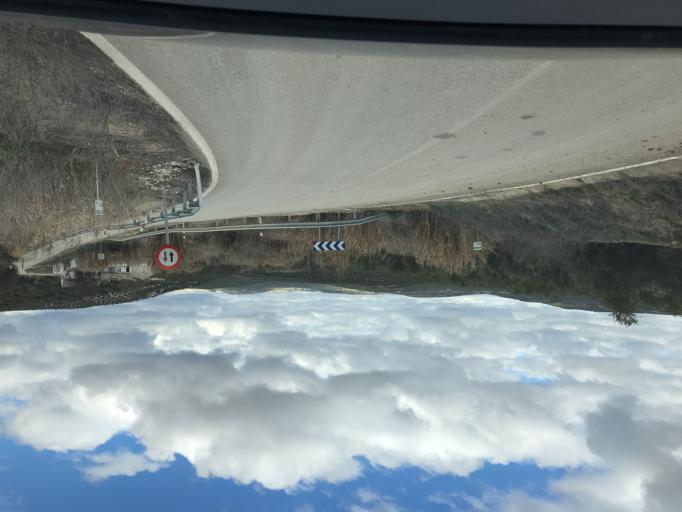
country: ES
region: Andalusia
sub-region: Provincia de Jaen
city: Baeza
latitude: 37.9553
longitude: -3.4317
